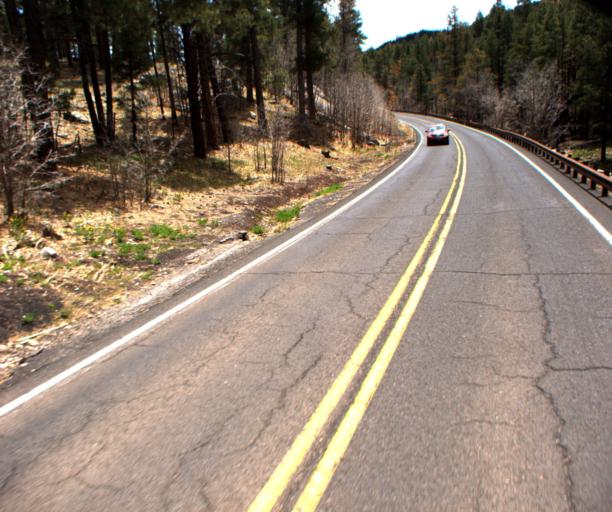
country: US
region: Arizona
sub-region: Coconino County
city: Kachina Village
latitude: 35.0982
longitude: -111.7328
